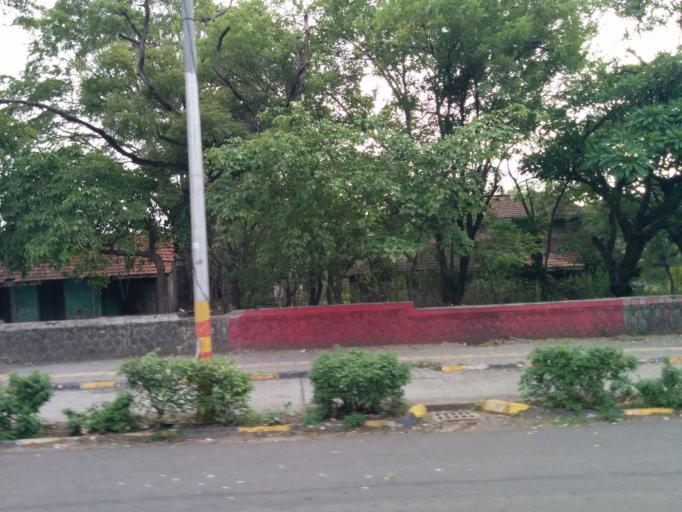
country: IN
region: Maharashtra
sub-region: Pune Division
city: Pune
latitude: 18.5040
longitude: 73.8785
